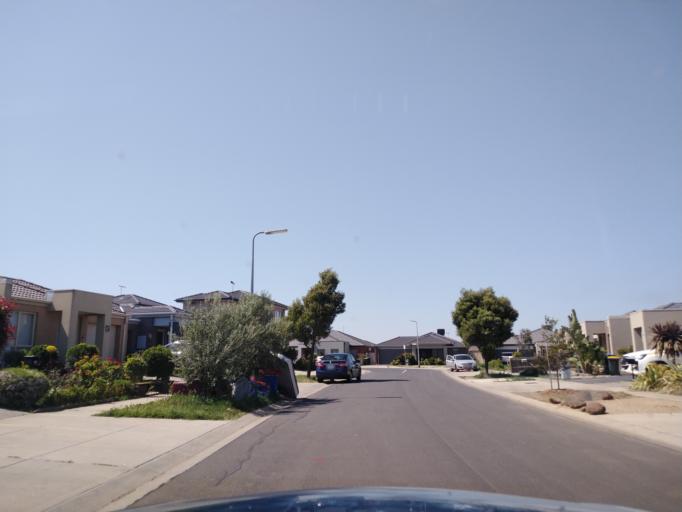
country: AU
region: Victoria
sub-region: Wyndham
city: Williams Landing
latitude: -37.8389
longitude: 144.7204
